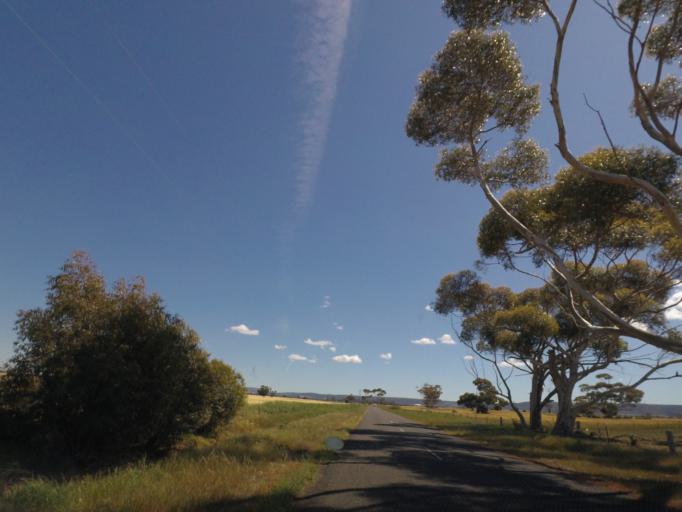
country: AU
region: Victoria
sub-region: Moorabool
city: Bacchus Marsh
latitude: -37.8028
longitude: 144.3740
